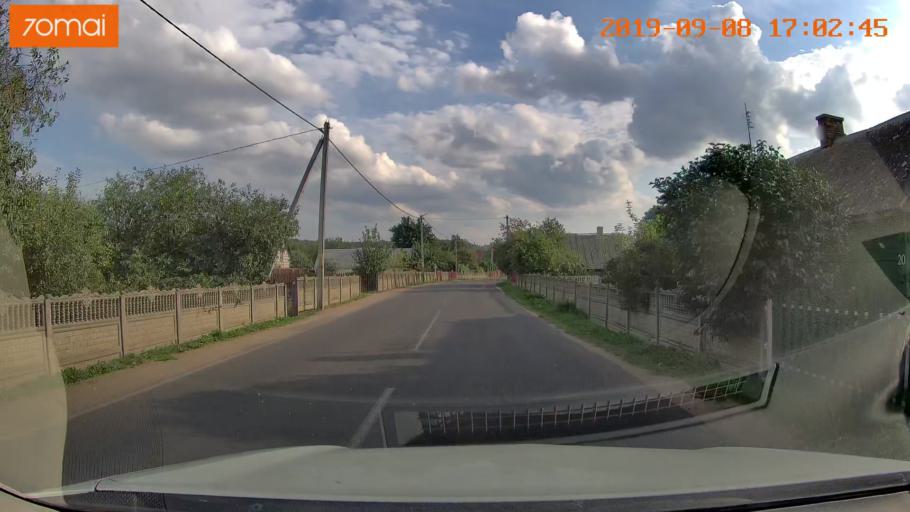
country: BY
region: Grodnenskaya
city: Hrodna
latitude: 53.7007
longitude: 23.9403
